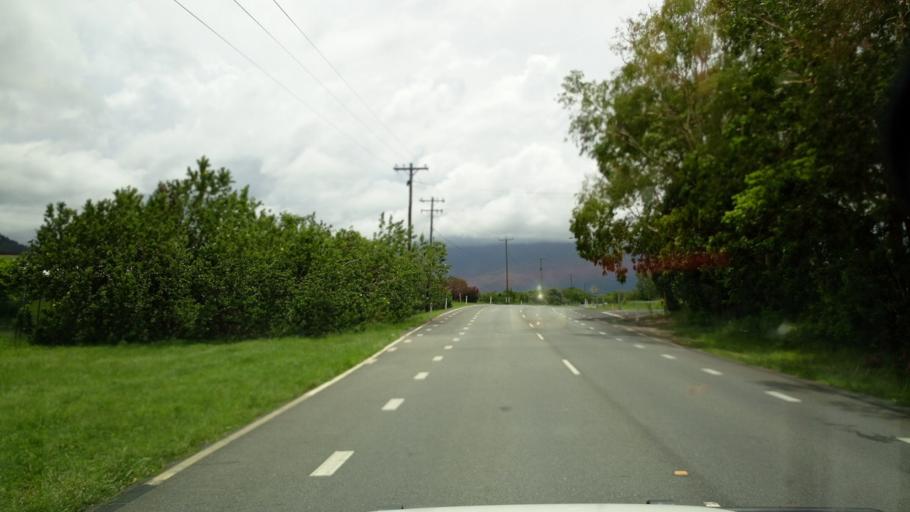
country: AU
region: Queensland
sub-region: Cairns
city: Redlynch
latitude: -16.8581
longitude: 145.7397
